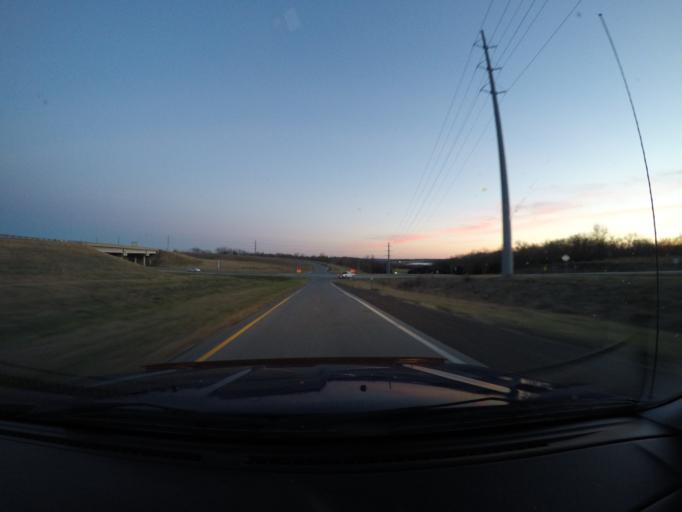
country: US
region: Kansas
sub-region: Douglas County
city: Lawrence
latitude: 38.9441
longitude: -95.3372
